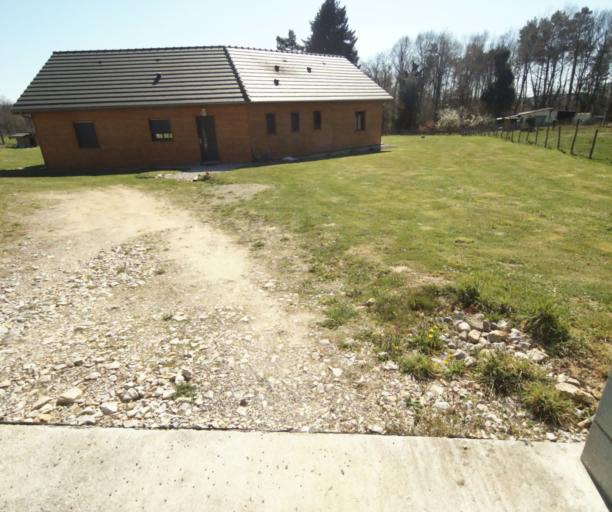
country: FR
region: Limousin
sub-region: Departement de la Correze
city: Saint-Mexant
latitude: 45.3055
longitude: 1.6795
